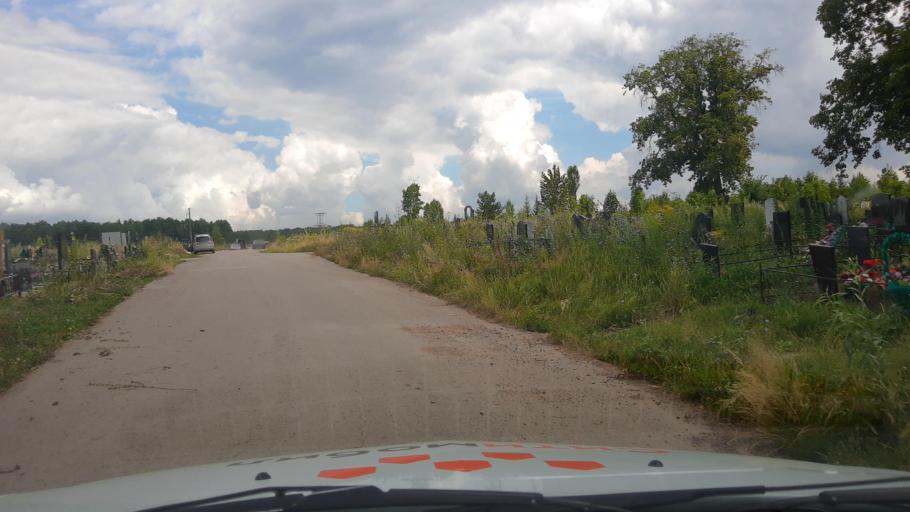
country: RU
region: Bashkortostan
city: Mikhaylovka
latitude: 54.8130
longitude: 55.8619
